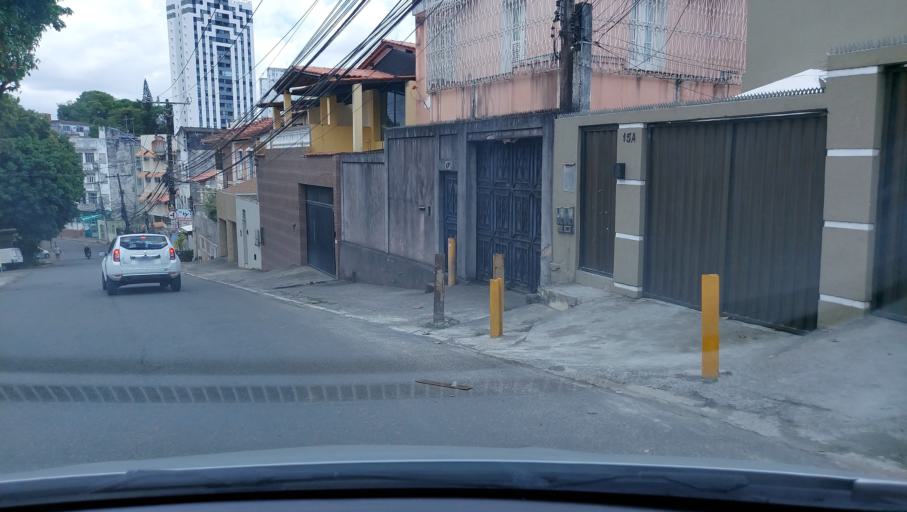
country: BR
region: Bahia
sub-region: Salvador
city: Salvador
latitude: -12.9735
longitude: -38.4914
